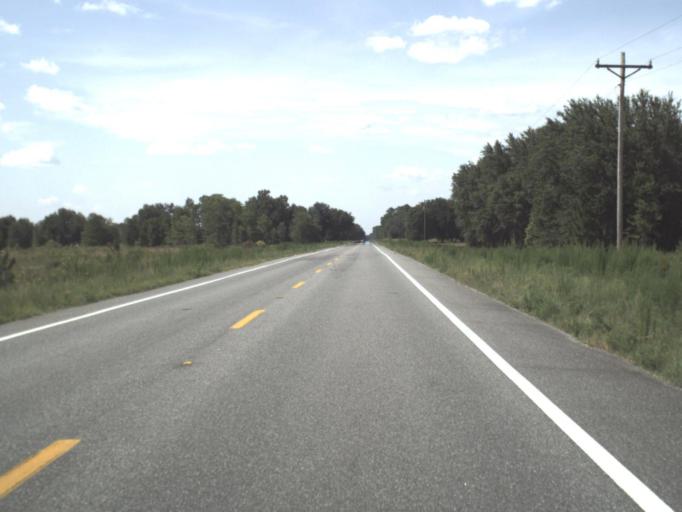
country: US
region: Florida
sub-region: Alachua County
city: High Springs
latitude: 29.8249
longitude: -82.7415
